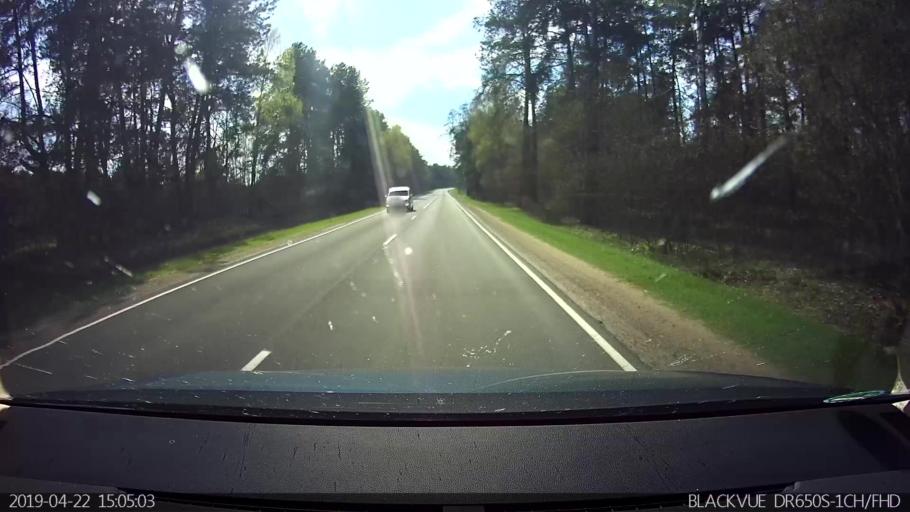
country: BY
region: Brest
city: Kamyanyets
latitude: 52.3360
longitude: 23.8778
